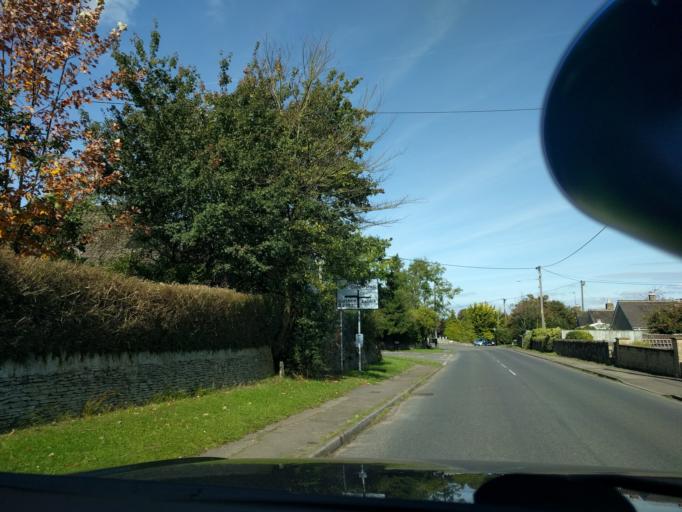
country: GB
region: England
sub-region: Wiltshire
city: Corsham
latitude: 51.4149
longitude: -2.1680
